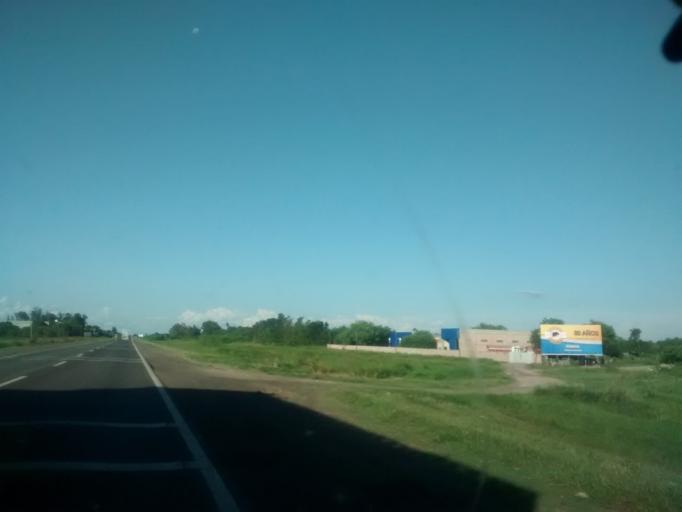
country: AR
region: Chaco
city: Fontana
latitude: -27.4735
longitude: -59.0541
